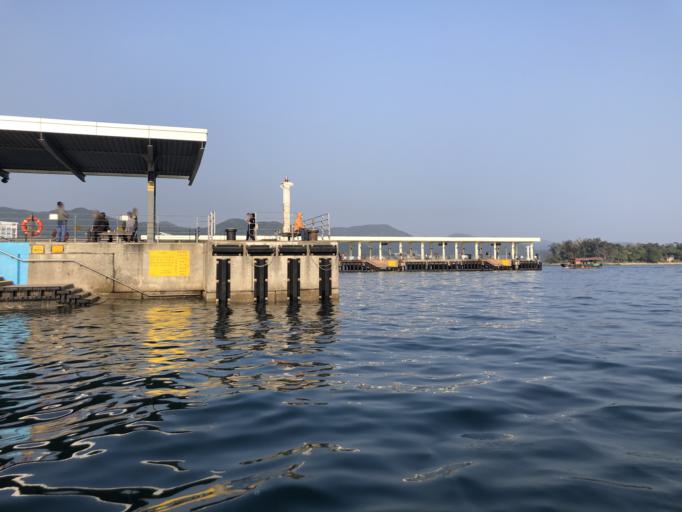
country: HK
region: Sai Kung
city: Sai Kung
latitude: 22.3809
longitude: 114.2746
